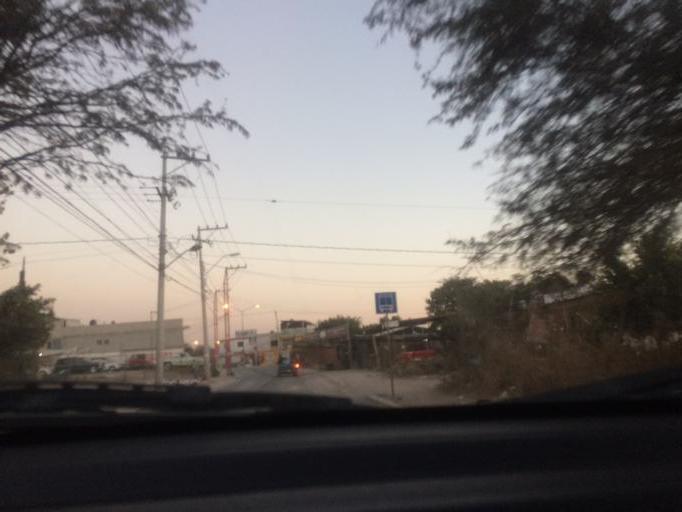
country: MX
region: Guanajuato
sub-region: Leon
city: Fraccionamiento Paraiso Real
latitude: 21.1189
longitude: -101.5890
